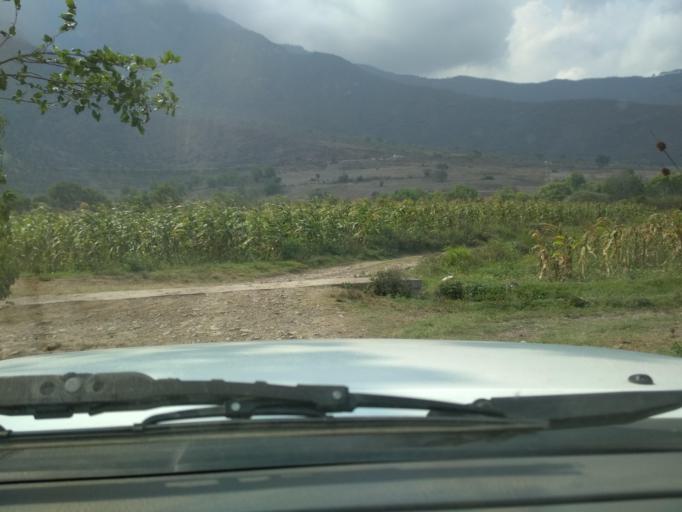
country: MX
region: Veracruz
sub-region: Acultzingo
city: Sierra de Agua
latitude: 18.7568
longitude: -97.2353
